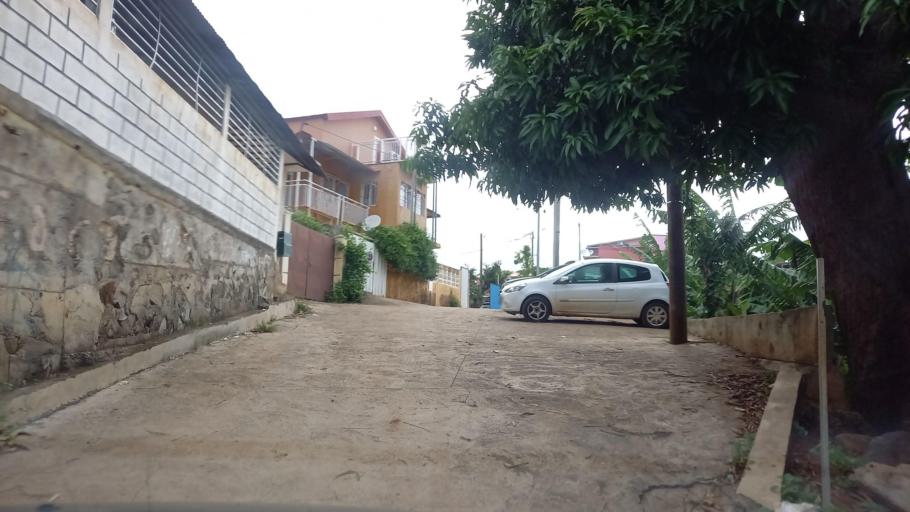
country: YT
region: Sada
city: Sada
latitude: -12.8530
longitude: 45.0960
